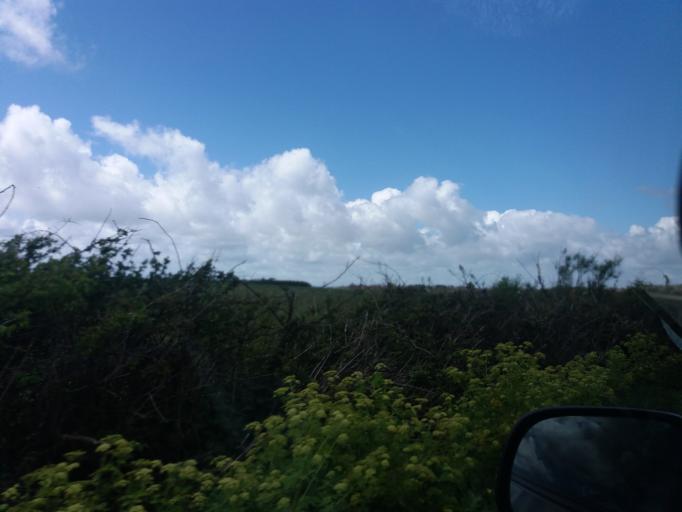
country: IE
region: Munster
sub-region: Waterford
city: Dunmore East
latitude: 52.2057
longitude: -6.8975
